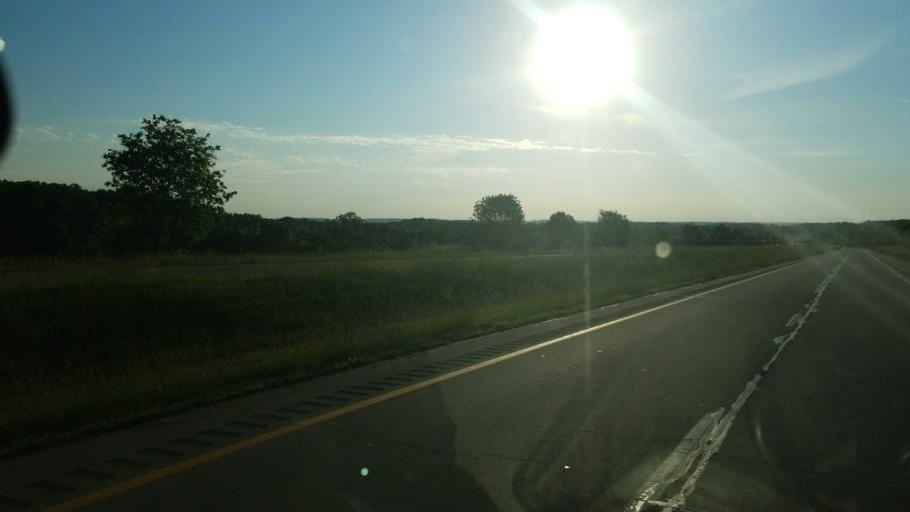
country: US
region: Ohio
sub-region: Ashland County
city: Ashland
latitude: 40.7846
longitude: -82.2835
